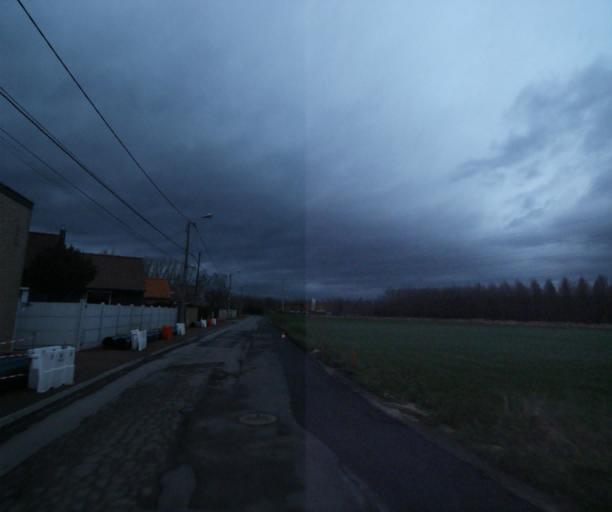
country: FR
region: Nord-Pas-de-Calais
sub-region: Departement du Nord
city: Anzin
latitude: 50.3901
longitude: 3.5169
